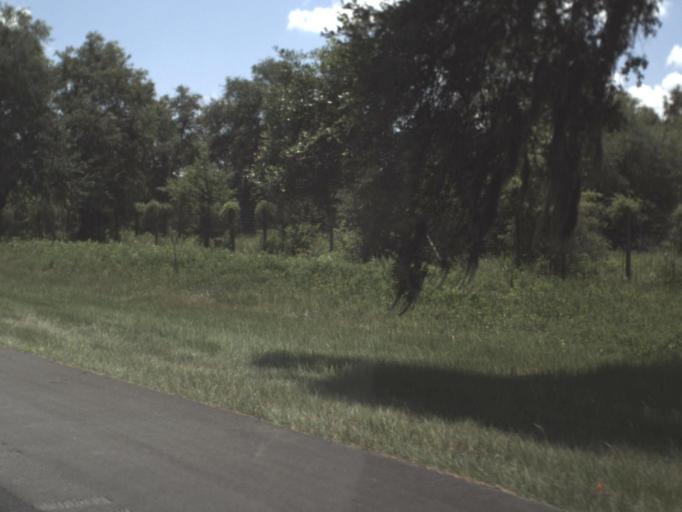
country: US
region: Florida
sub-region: Madison County
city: Madison
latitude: 30.3945
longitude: -83.3496
